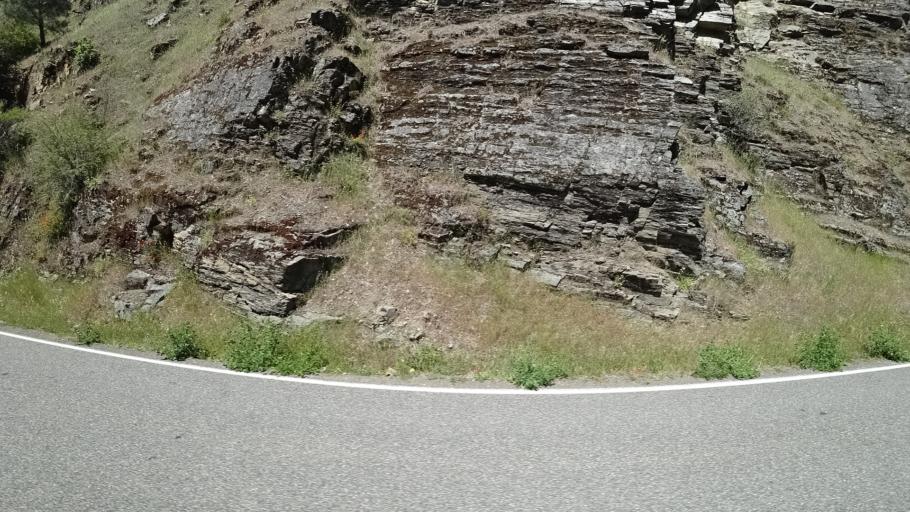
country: US
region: California
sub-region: Trinity County
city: Weaverville
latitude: 40.7637
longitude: -123.1397
